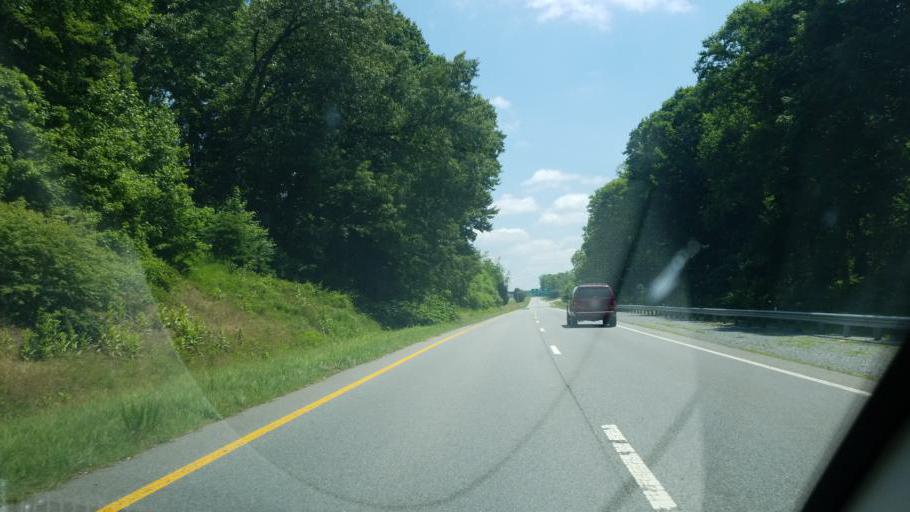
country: US
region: Virginia
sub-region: Campbell County
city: Altavista
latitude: 37.1246
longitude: -79.3153
